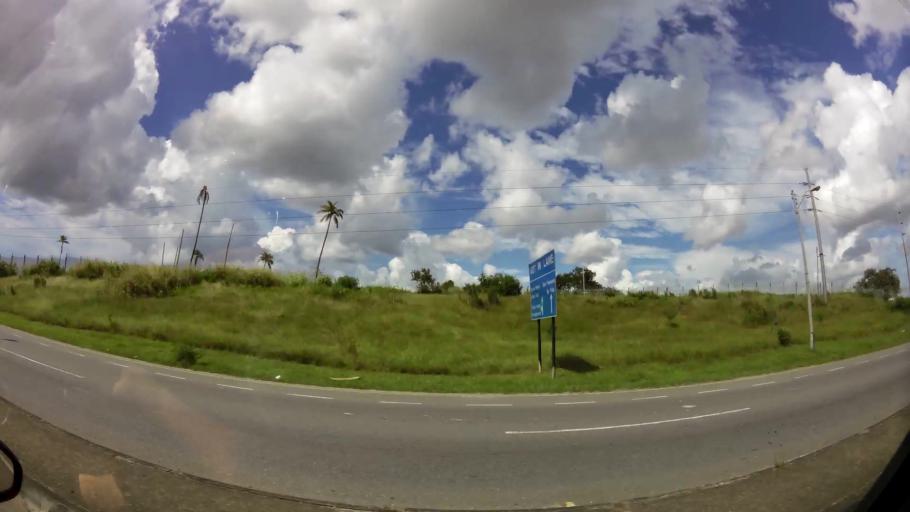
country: TT
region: City of San Fernando
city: San Fernando
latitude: 10.2599
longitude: -61.4626
